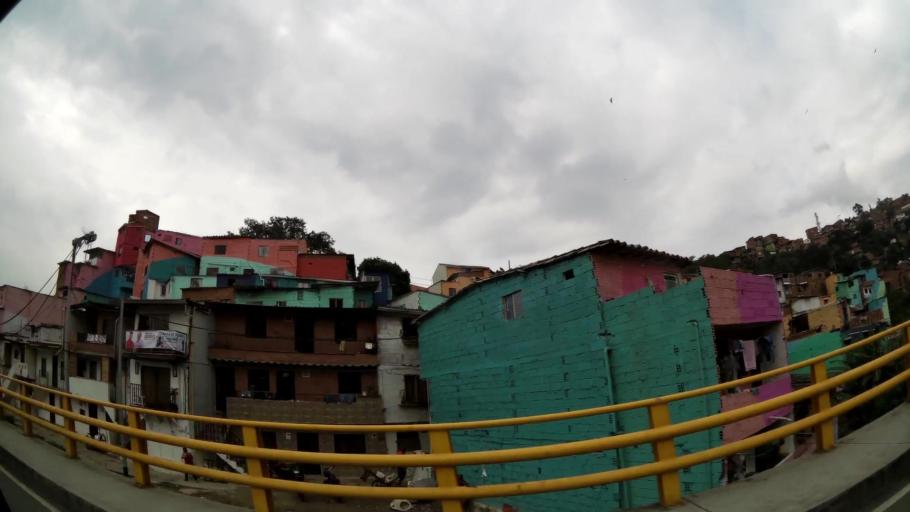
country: CO
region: Antioquia
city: Medellin
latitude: 6.2727
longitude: -75.5956
